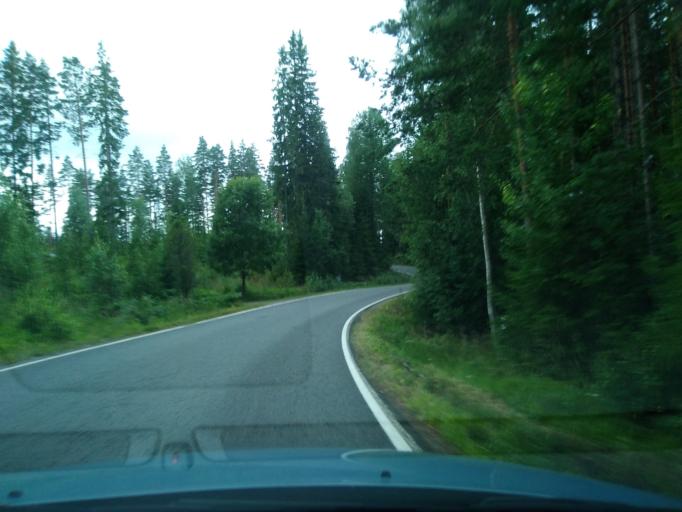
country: FI
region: Uusimaa
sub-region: Helsinki
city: Kaerkoelae
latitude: 60.7795
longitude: 24.0744
